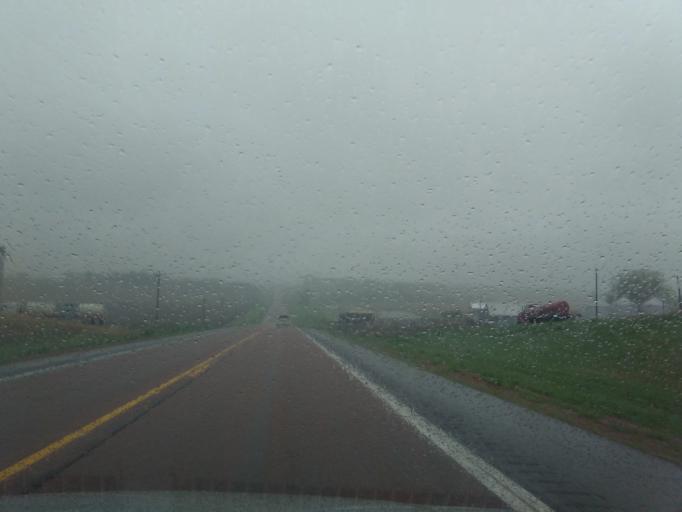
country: US
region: Nebraska
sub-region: Wayne County
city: Wayne
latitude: 42.2355
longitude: -97.1626
